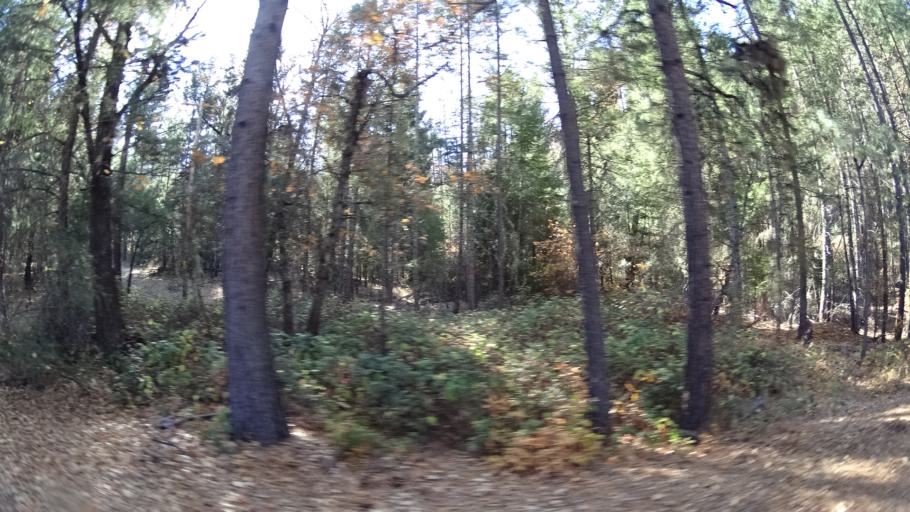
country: US
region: California
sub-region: Siskiyou County
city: Yreka
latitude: 41.8218
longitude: -122.9736
